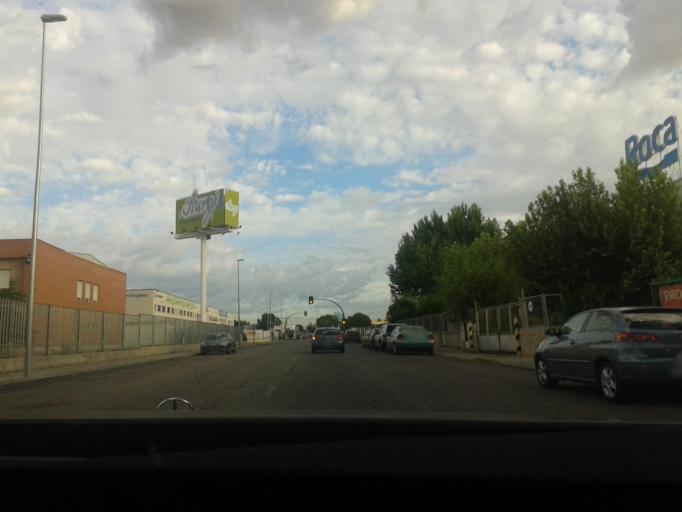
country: ES
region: Madrid
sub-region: Provincia de Madrid
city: Alcala de Henares
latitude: 40.4885
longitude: -3.3831
